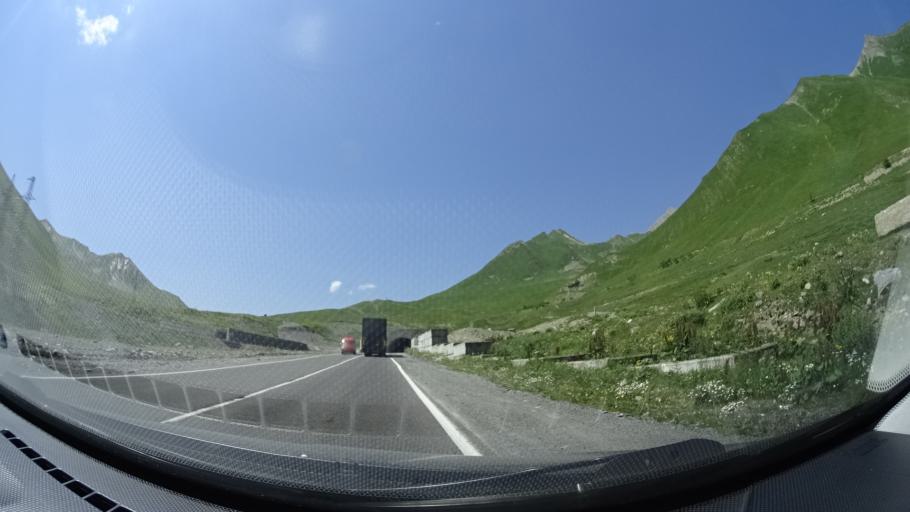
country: GE
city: Gudauri
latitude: 42.5260
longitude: 44.4694
